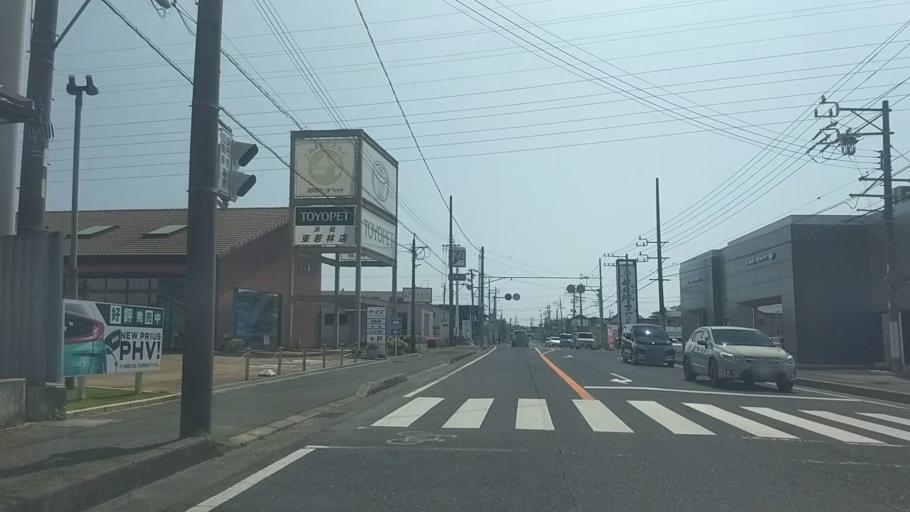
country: JP
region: Shizuoka
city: Hamamatsu
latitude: 34.6910
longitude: 137.7157
